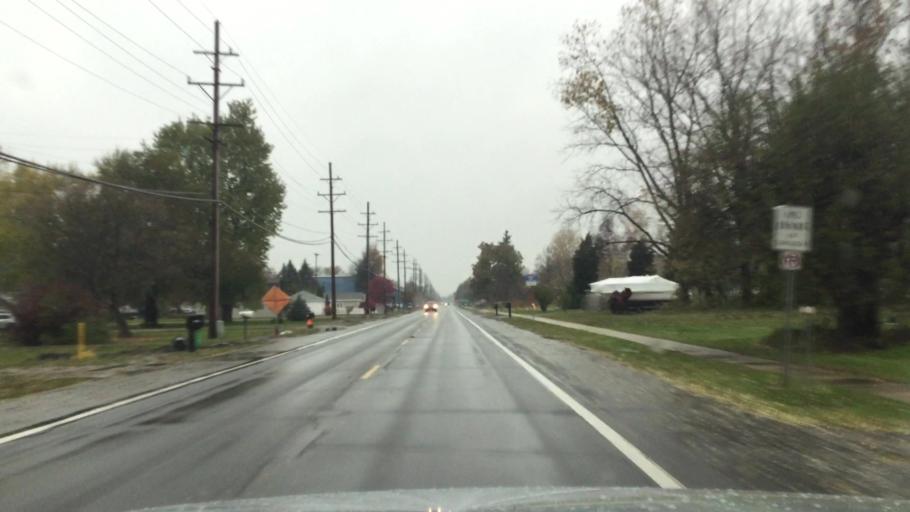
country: US
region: Michigan
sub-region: Saint Clair County
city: Pearl Beach
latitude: 42.6235
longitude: -82.5892
